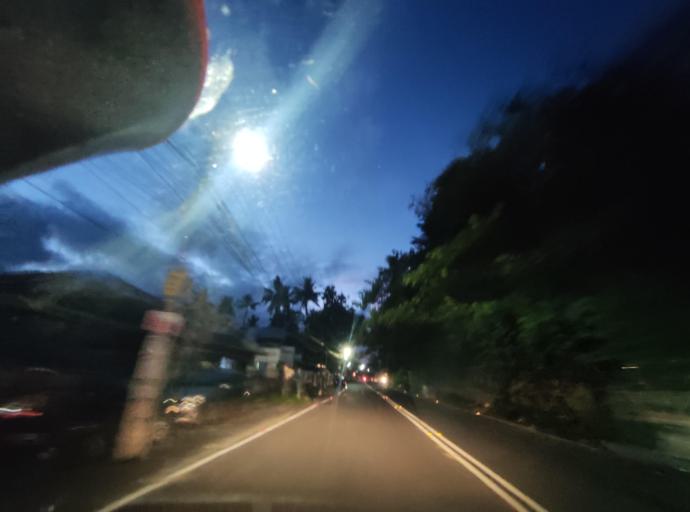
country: IN
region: Kerala
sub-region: Thiruvananthapuram
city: Thiruvananthapuram
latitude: 8.5442
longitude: 76.9603
